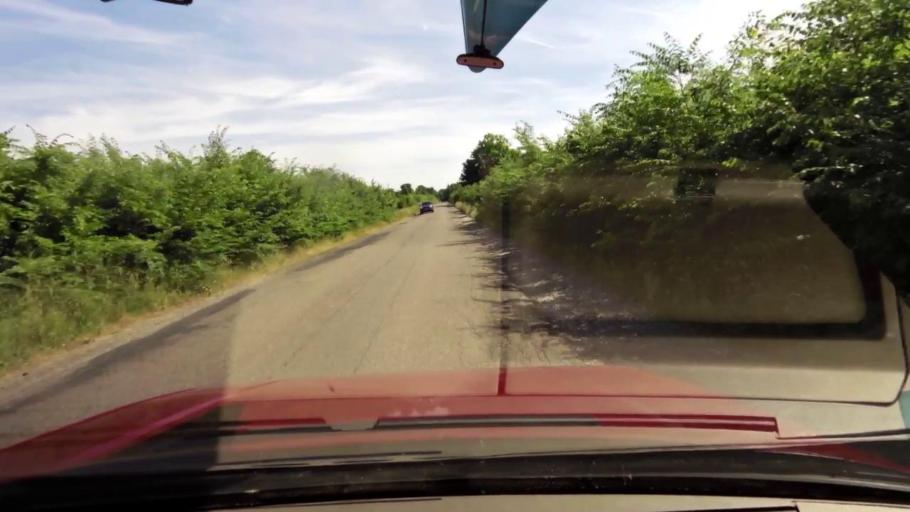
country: PL
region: Pomeranian Voivodeship
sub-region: Powiat slupski
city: Kobylnica
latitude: 54.3615
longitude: 16.9677
